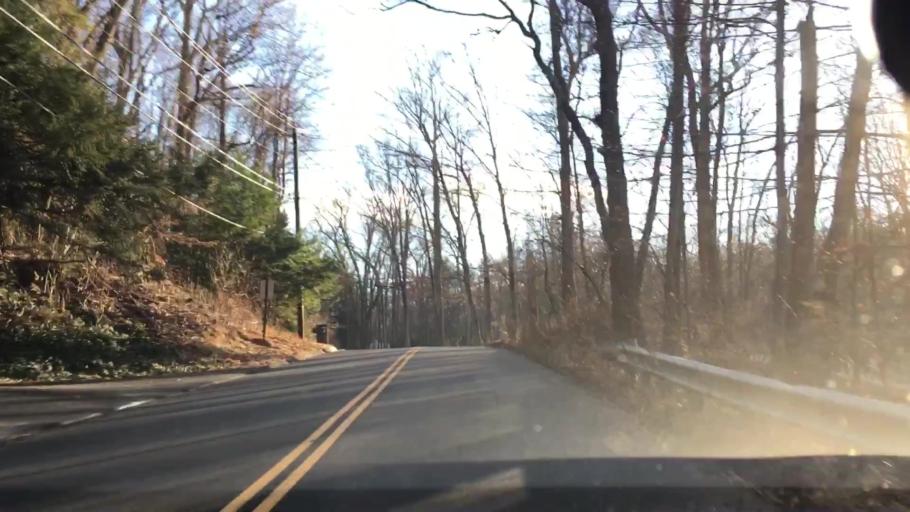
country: US
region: Connecticut
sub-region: Fairfield County
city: Newtown
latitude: 41.4346
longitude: -73.3152
